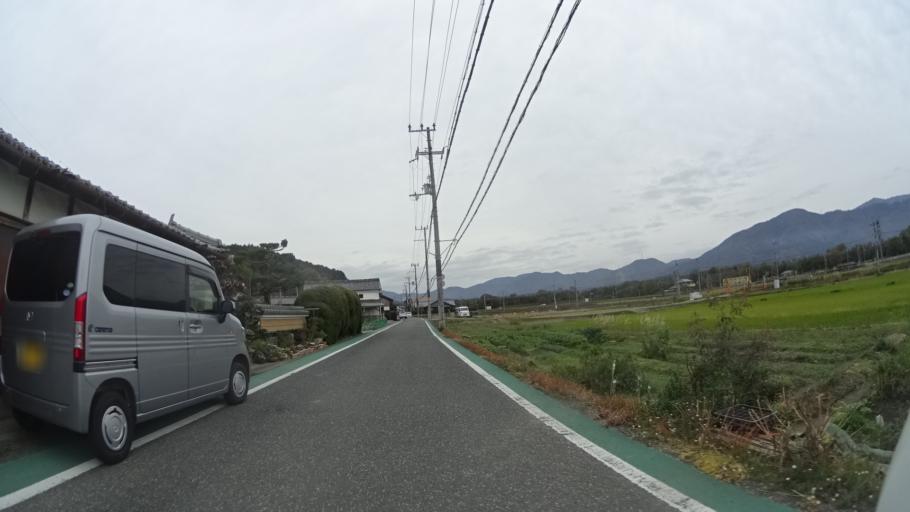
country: JP
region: Kyoto
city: Kameoka
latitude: 35.0570
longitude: 135.5445
